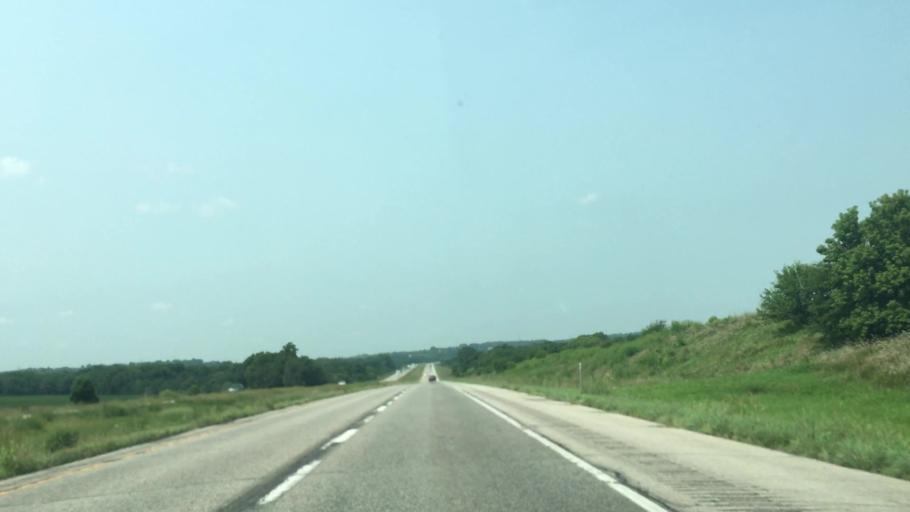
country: US
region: Iowa
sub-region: Linn County
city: Center Point
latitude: 42.1885
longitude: -91.8060
